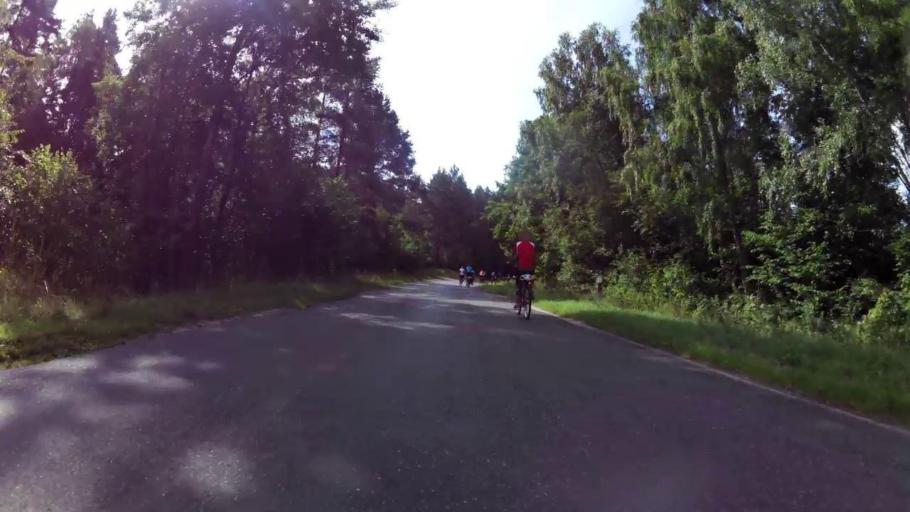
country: PL
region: West Pomeranian Voivodeship
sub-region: Powiat drawski
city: Drawsko Pomorskie
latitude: 53.4785
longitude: 15.7780
